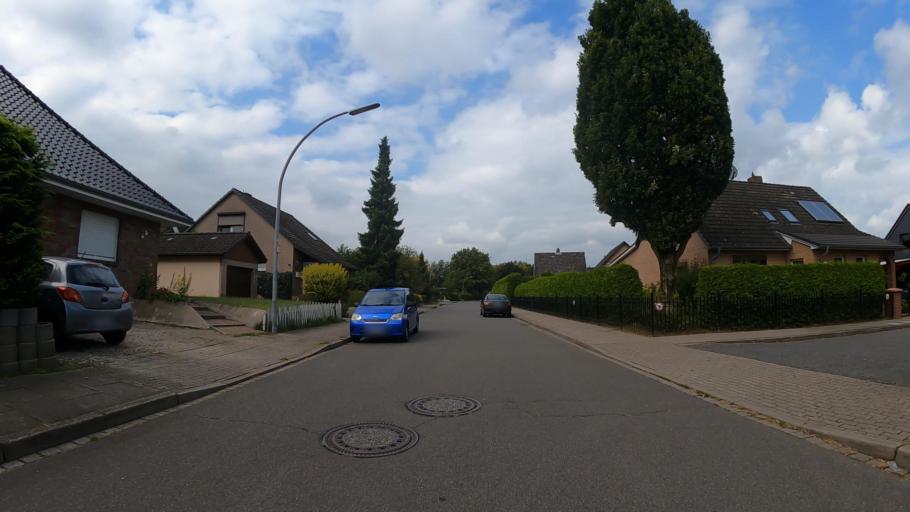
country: DE
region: Schleswig-Holstein
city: Elmshorn
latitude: 53.7402
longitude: 9.6659
